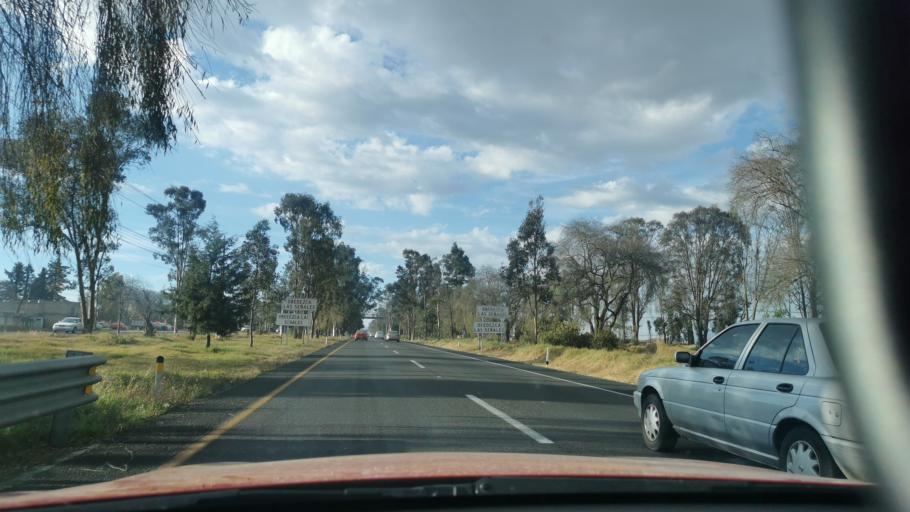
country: MX
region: Mexico
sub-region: Toluca
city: Colonia Aviacion Autopan
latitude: 19.3734
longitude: -99.6980
